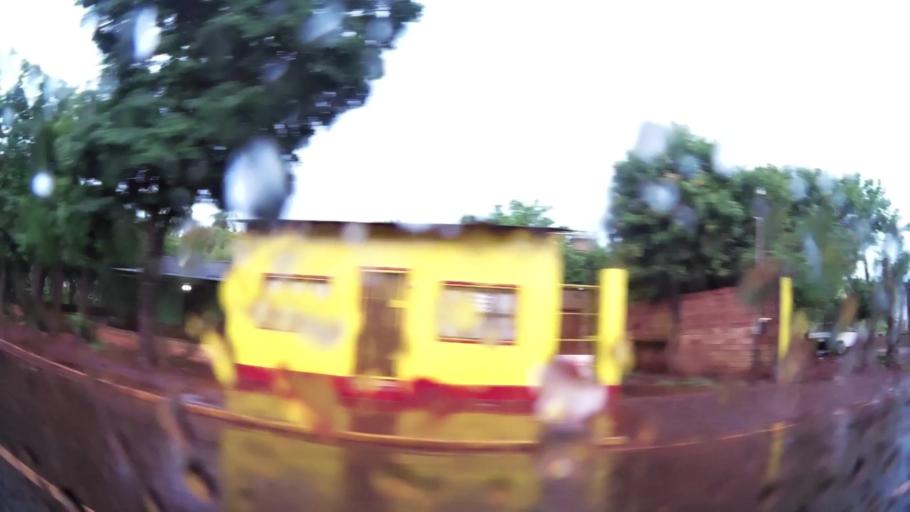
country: PY
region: Alto Parana
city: Presidente Franco
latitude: -25.5422
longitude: -54.6784
